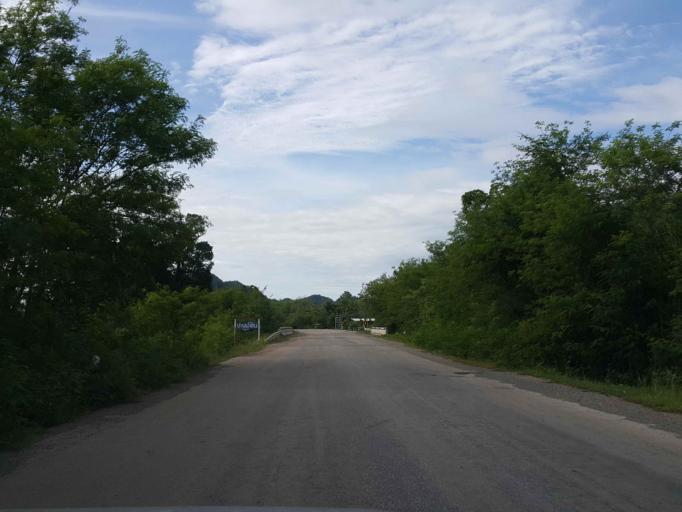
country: TH
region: Sukhothai
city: Thung Saliam
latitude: 17.2737
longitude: 99.5309
